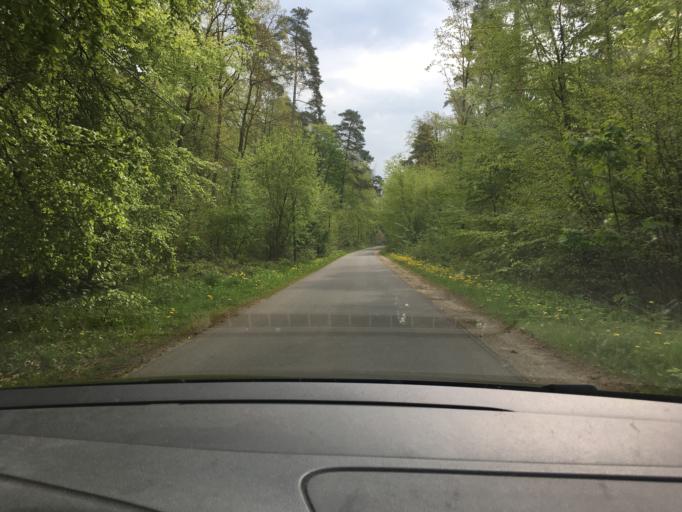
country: DE
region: Mecklenburg-Vorpommern
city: Krakow am See
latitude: 53.6694
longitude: 12.2941
